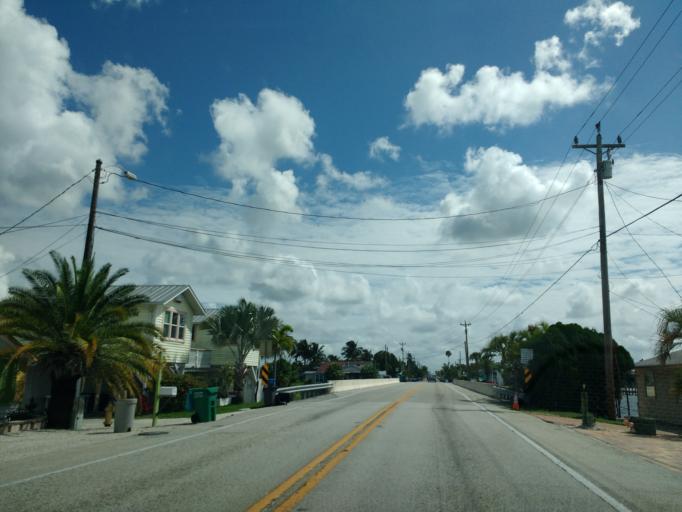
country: US
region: Florida
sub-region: Lee County
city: Pine Island Center
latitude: 26.6252
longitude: -82.0746
